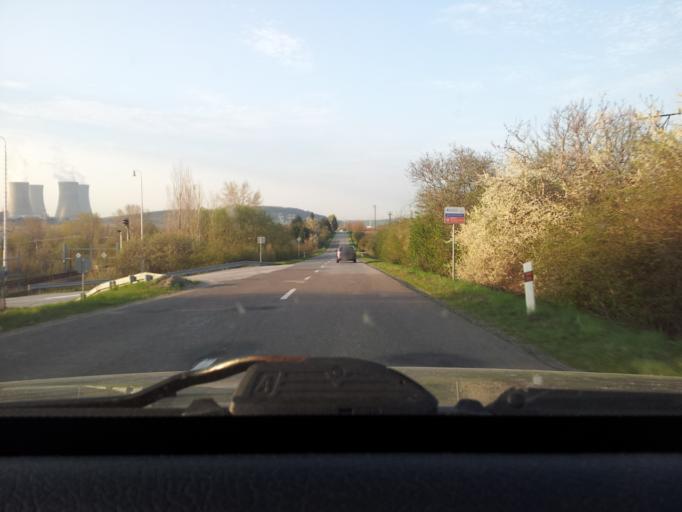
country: SK
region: Nitriansky
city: Tlmace
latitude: 48.2713
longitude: 18.4466
